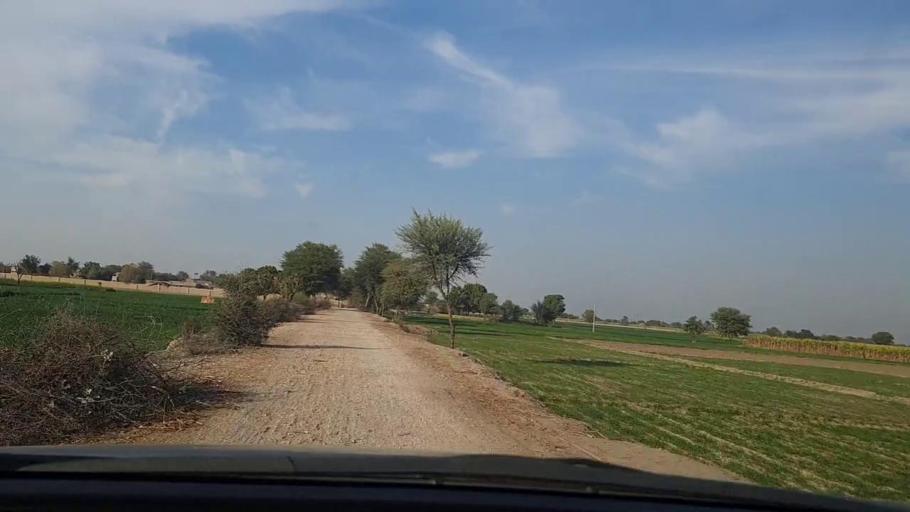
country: PK
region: Sindh
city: Daulatpur
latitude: 26.3157
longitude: 68.0204
